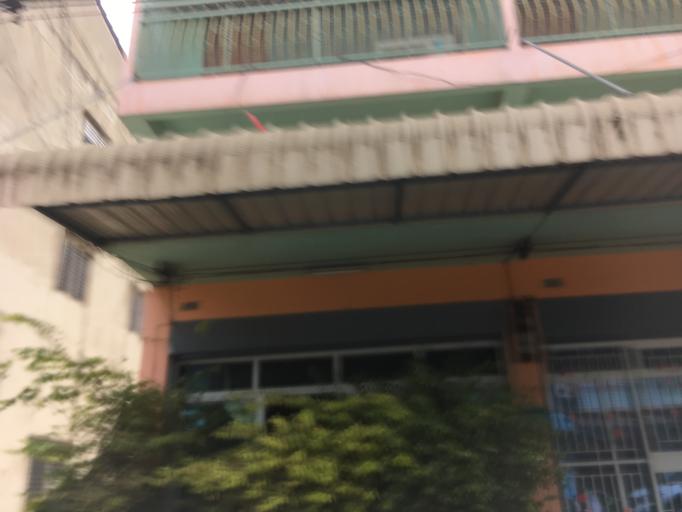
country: TH
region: Chachoengsao
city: Bang Khla
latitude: 13.7268
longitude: 101.2083
